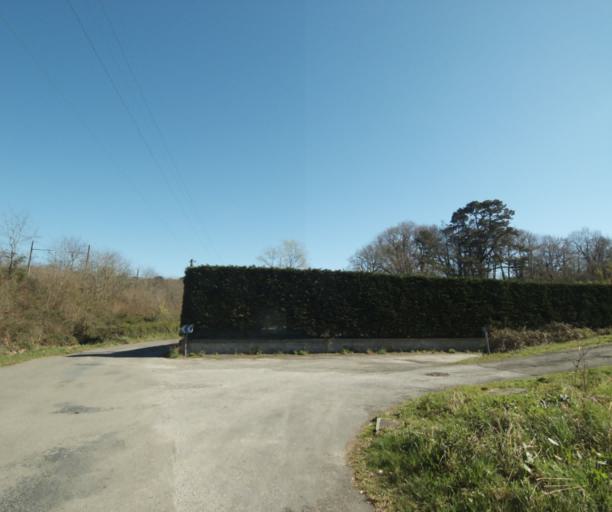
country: FR
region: Aquitaine
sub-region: Departement des Pyrenees-Atlantiques
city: Ciboure
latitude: 43.3809
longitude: -1.6931
